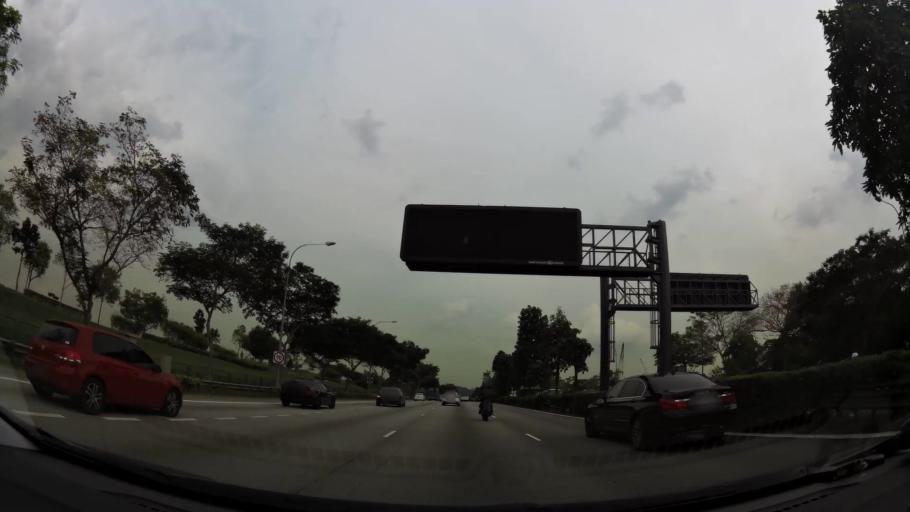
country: MY
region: Johor
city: Johor Bahru
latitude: 1.4247
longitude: 103.7912
